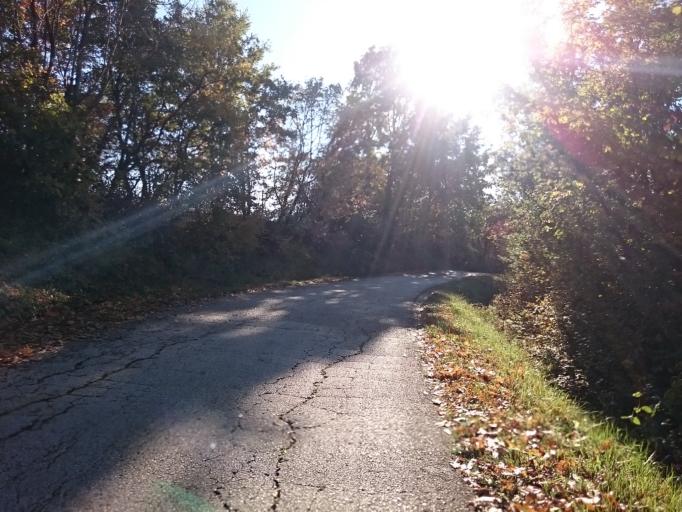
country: HR
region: Istarska
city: Buje
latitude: 45.4249
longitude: 13.7385
